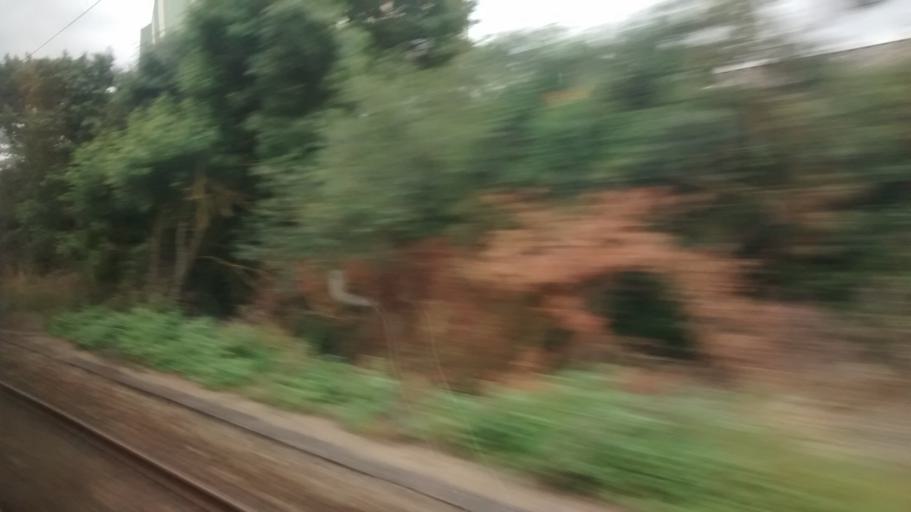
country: FR
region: Pays de la Loire
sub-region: Departement de la Mayenne
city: Laval
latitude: 48.0784
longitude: -0.7409
